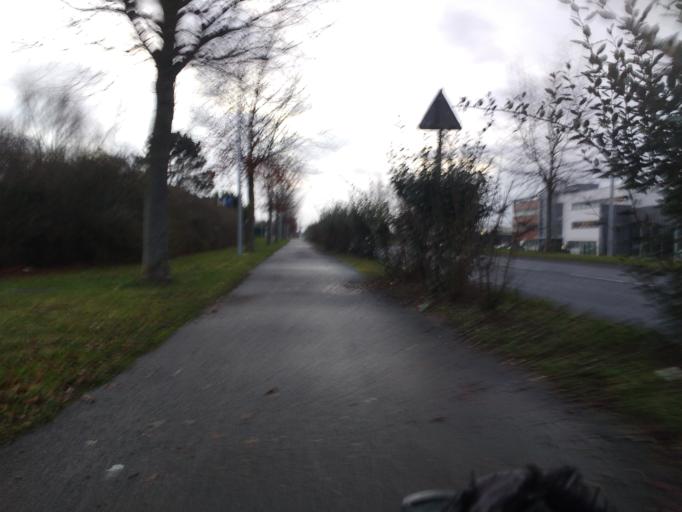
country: FR
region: Picardie
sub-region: Departement de la Somme
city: Longueau
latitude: 49.8658
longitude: 2.3698
